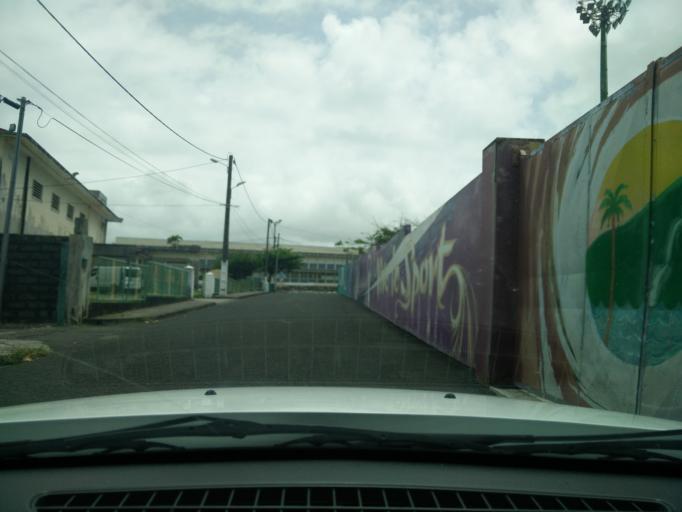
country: GP
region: Guadeloupe
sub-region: Guadeloupe
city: Capesterre-Belle-Eau
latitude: 16.0479
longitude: -61.5620
